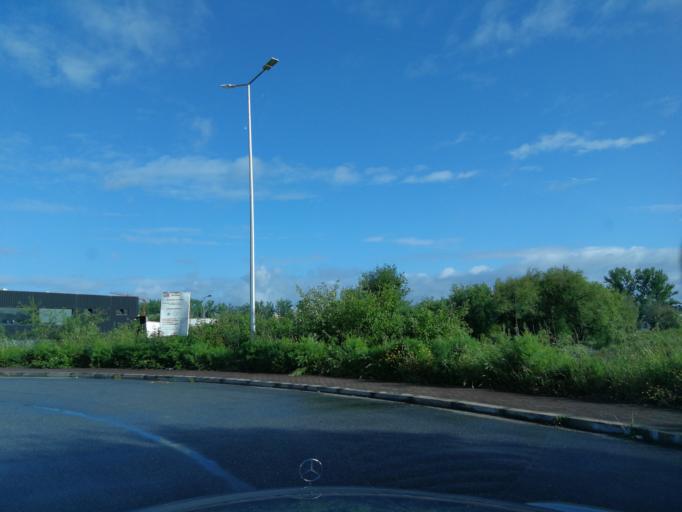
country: PT
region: Braga
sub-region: Braga
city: Braga
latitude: 41.5658
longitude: -8.4472
